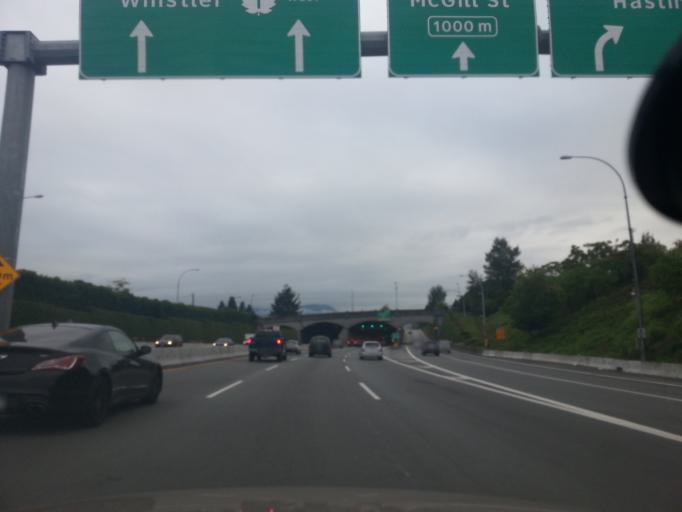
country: CA
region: British Columbia
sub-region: Fraser Valley Regional District
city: North Vancouver
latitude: 49.2758
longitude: -123.0313
